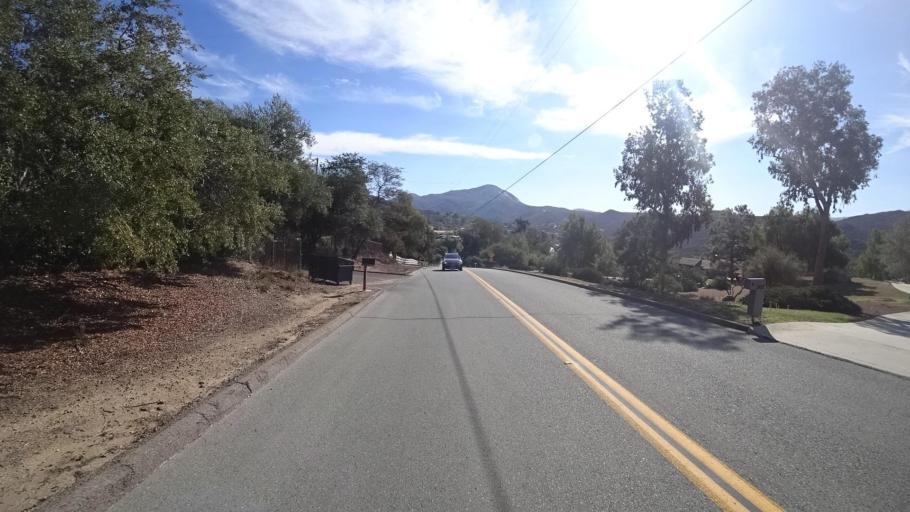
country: US
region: California
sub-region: San Diego County
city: Alpine
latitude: 32.8179
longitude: -116.7448
